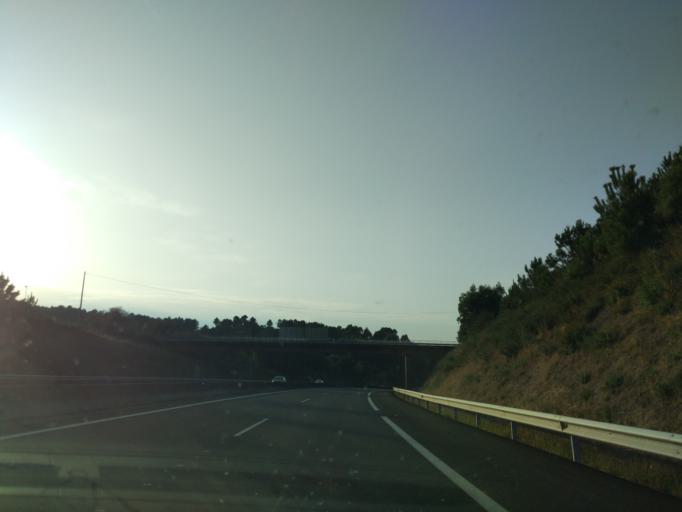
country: ES
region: Galicia
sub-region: Provincia de Pontevedra
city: Barro
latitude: 42.5231
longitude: -8.6677
